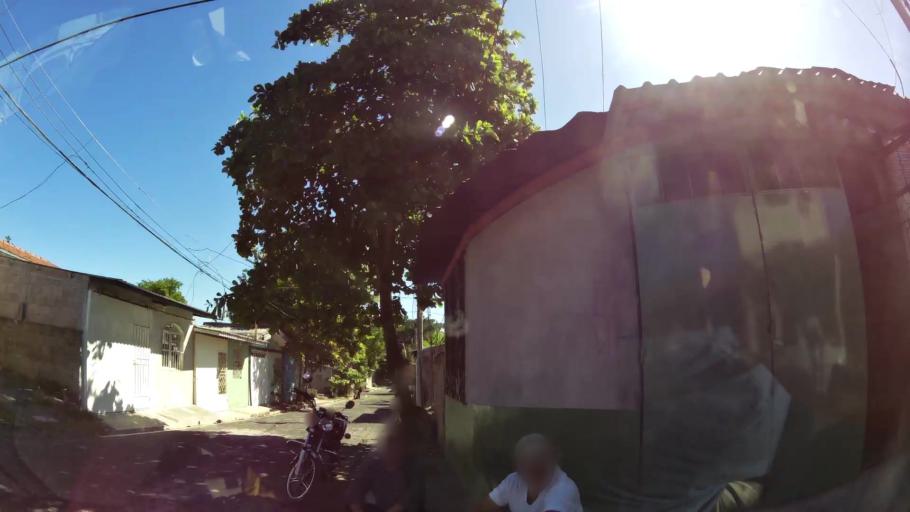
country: SV
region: San Miguel
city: San Miguel
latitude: 13.4630
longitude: -88.1604
